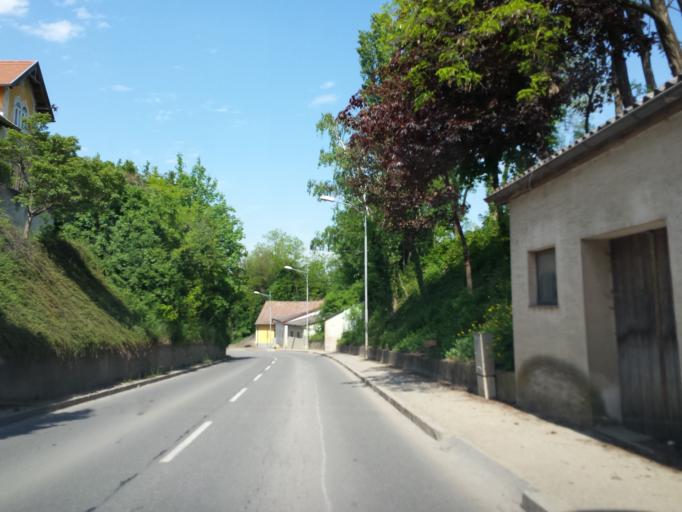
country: AT
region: Lower Austria
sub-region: Politischer Bezirk Tulln
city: Atzenbrugg
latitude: 48.3020
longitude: 15.8960
